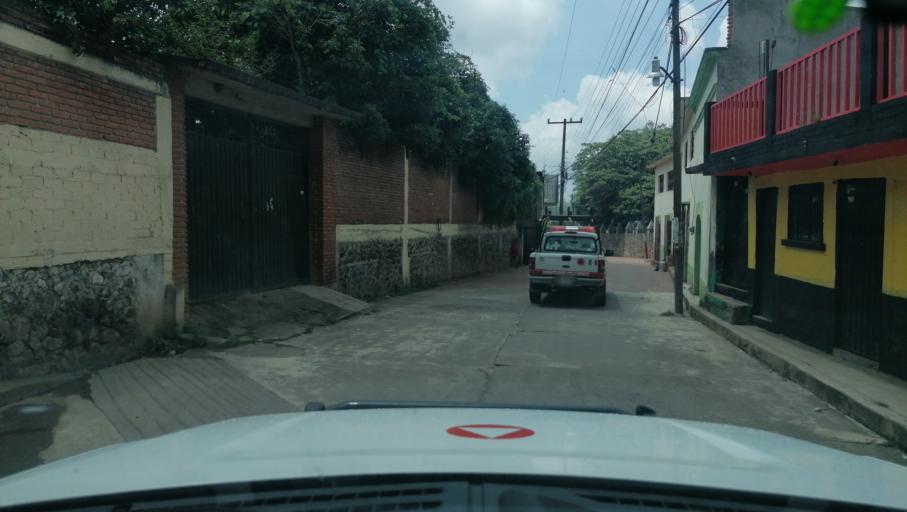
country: MX
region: Morelos
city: Ocuituco
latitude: 18.8828
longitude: -98.8167
